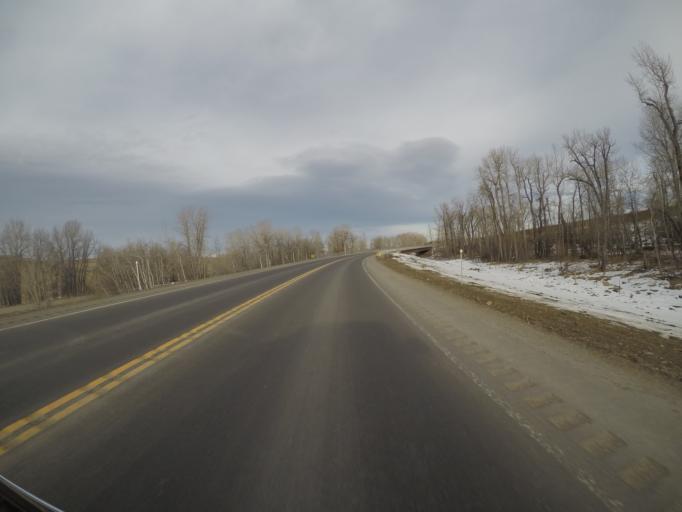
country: US
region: Montana
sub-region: Stillwater County
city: Absarokee
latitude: 45.4337
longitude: -109.4695
